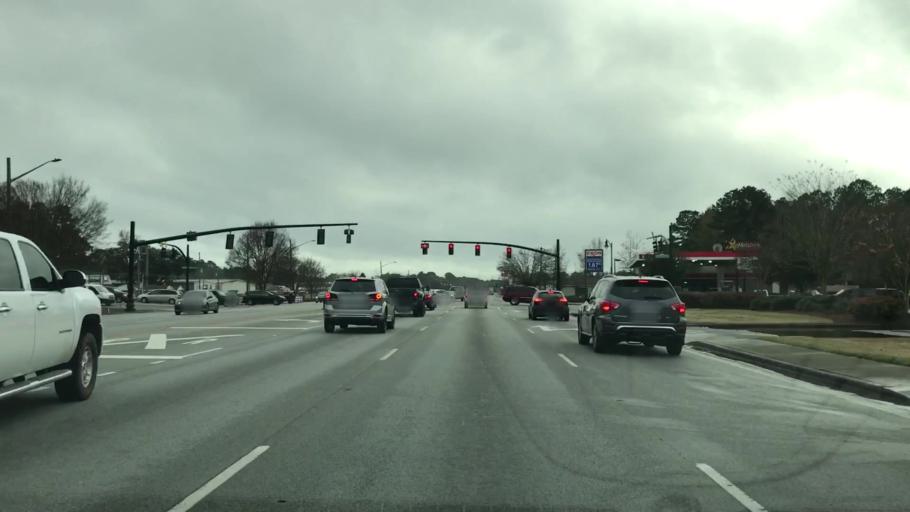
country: US
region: South Carolina
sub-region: Berkeley County
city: Goose Creek
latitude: 33.0019
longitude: -80.0381
